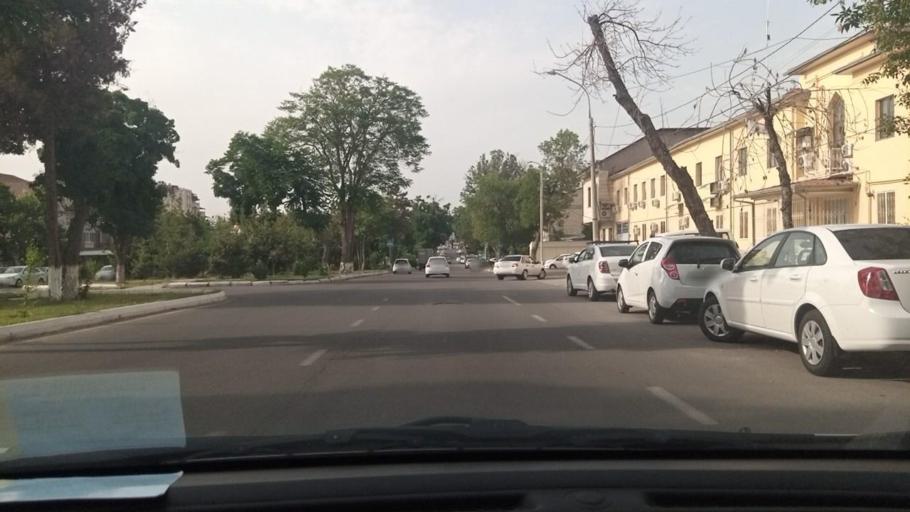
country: UZ
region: Toshkent Shahri
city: Tashkent
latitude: 41.3292
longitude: 69.2917
